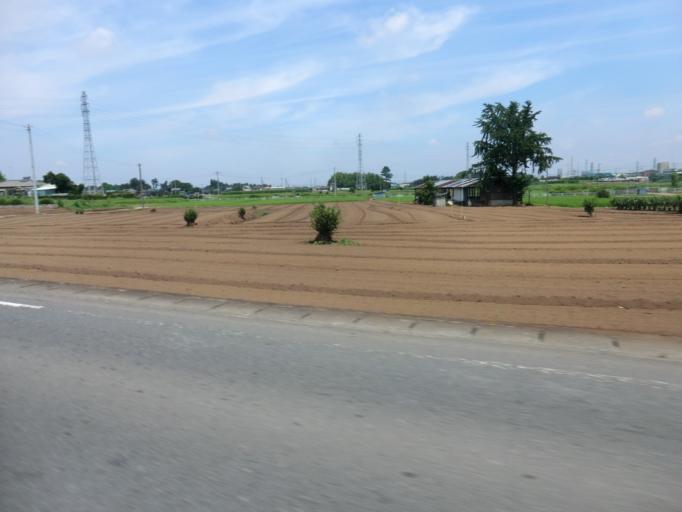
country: JP
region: Ibaraki
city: Sakai
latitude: 36.0990
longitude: 139.8097
